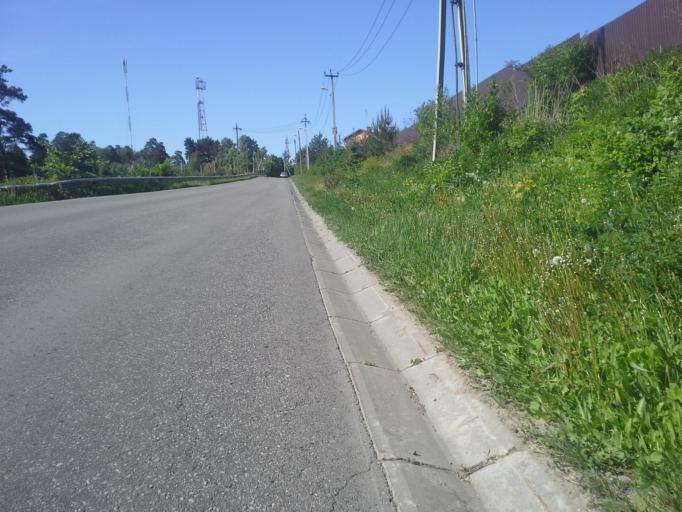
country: RU
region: Moskovskaya
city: Vatutinki
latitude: 55.4494
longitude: 37.3986
